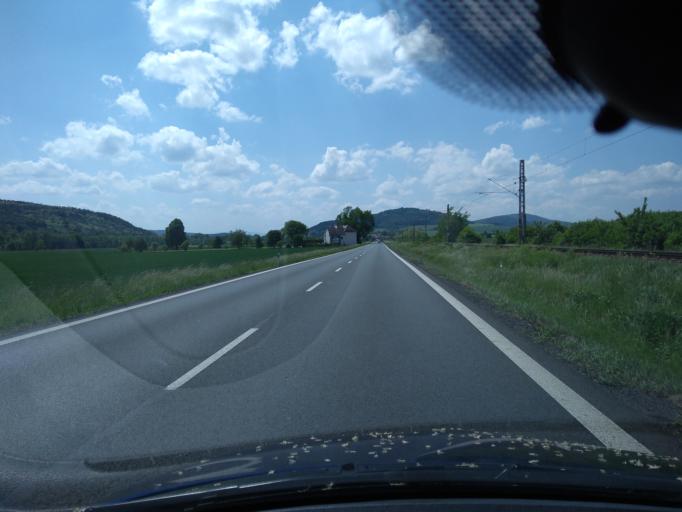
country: CZ
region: Plzensky
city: Prestice
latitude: 49.5360
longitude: 13.3065
